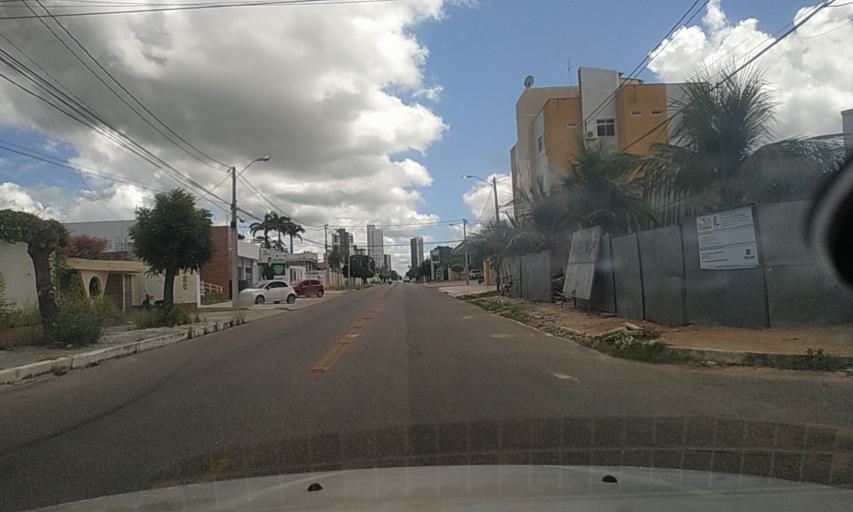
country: BR
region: Rio Grande do Norte
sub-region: Mossoro
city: Mossoro
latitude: -5.1840
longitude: -37.3538
